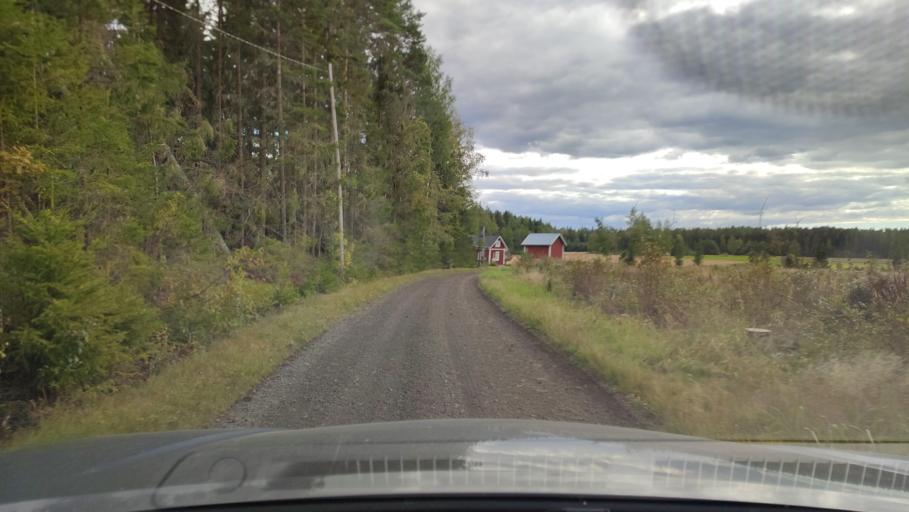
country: FI
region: Southern Ostrobothnia
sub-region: Suupohja
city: Karijoki
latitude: 62.2141
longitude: 21.5672
